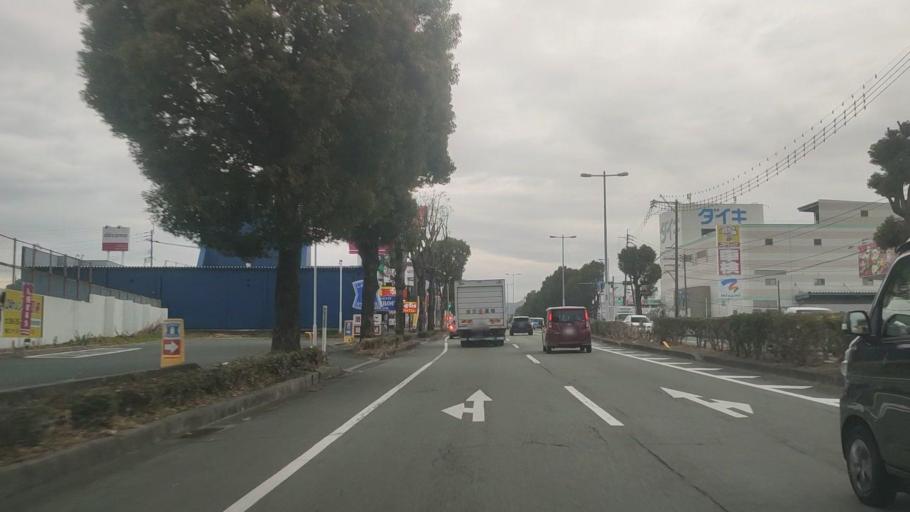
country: JP
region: Kumamoto
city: Kumamoto
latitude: 32.8248
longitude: 130.7635
